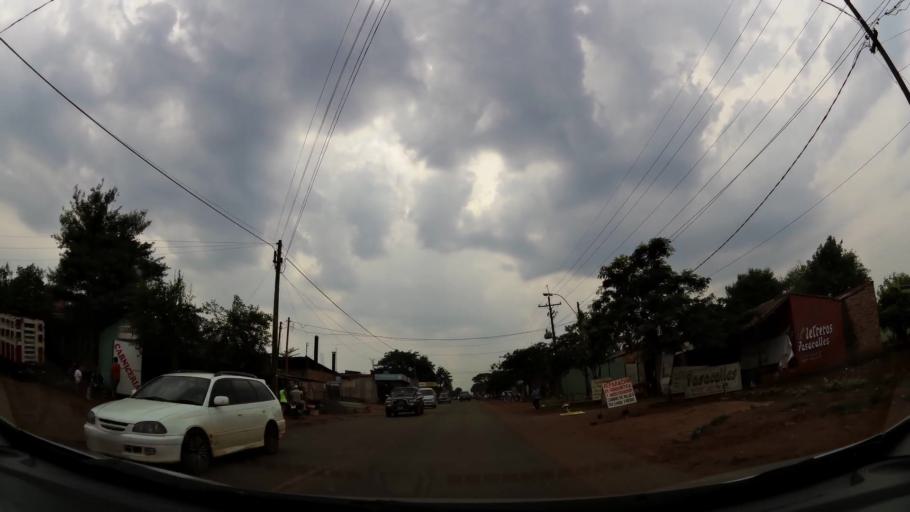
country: PY
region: Alto Parana
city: Presidente Franco
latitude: -25.5546
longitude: -54.6469
